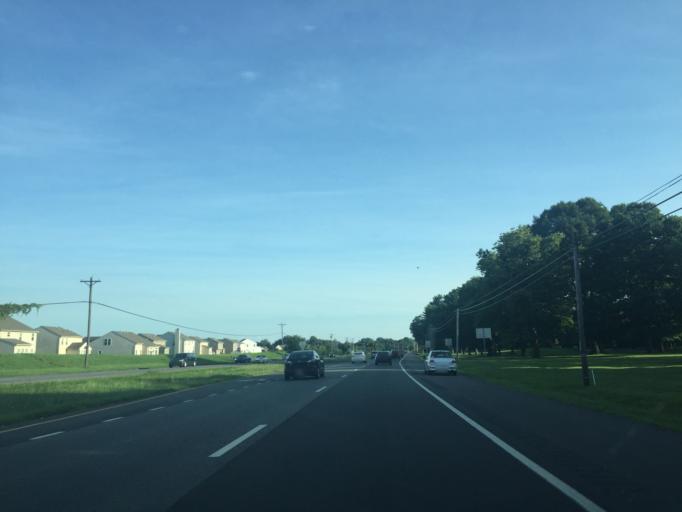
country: US
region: Delaware
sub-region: Kent County
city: Cheswold
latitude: 39.2530
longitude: -75.5866
